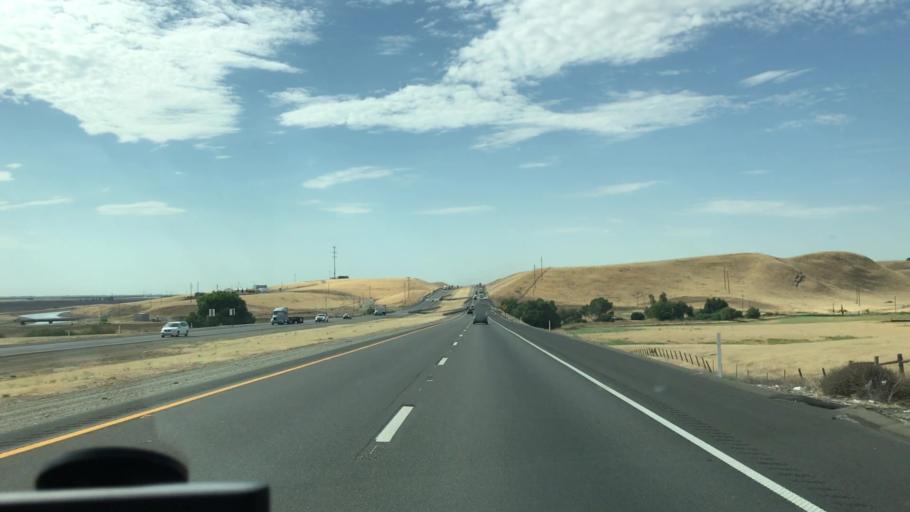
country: US
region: California
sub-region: Stanislaus County
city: Patterson
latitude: 37.4265
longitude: -121.1561
